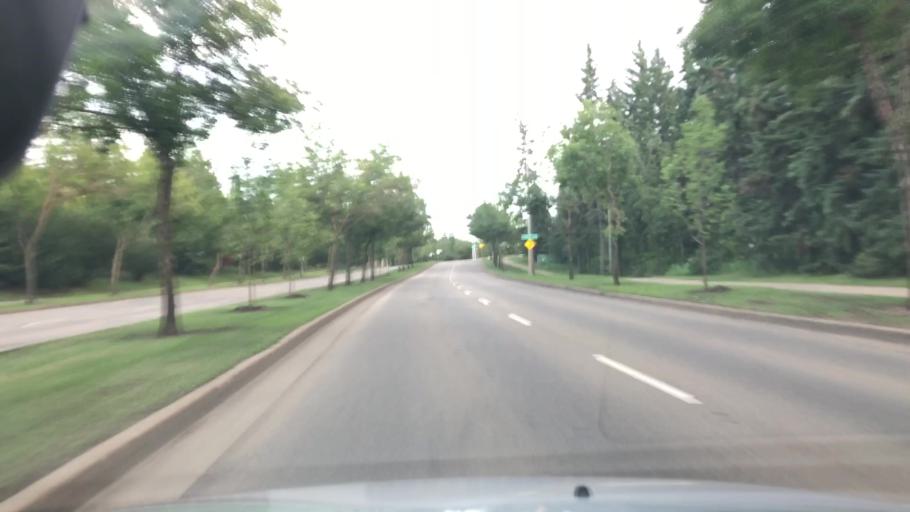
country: CA
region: Alberta
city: St. Albert
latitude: 53.6376
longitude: -113.5920
